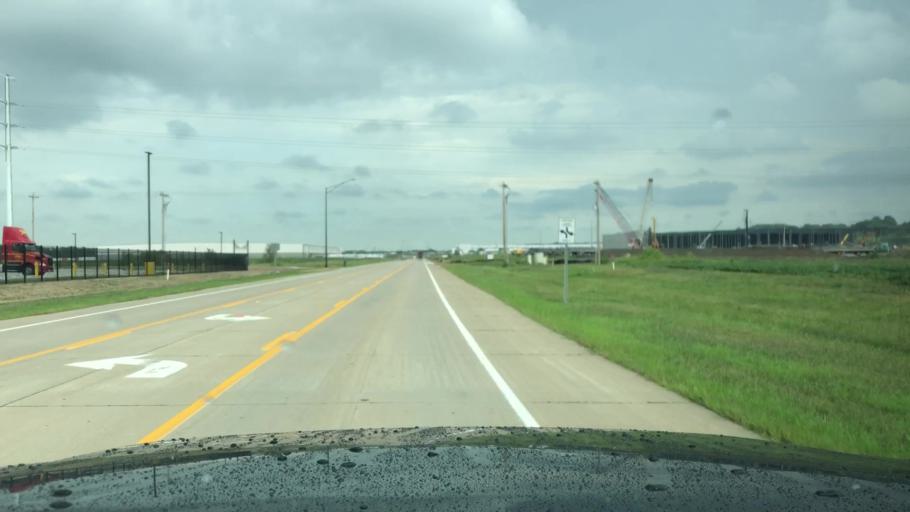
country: US
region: Missouri
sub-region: Saint Charles County
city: Saint Peters
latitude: 38.8102
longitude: -90.5778
